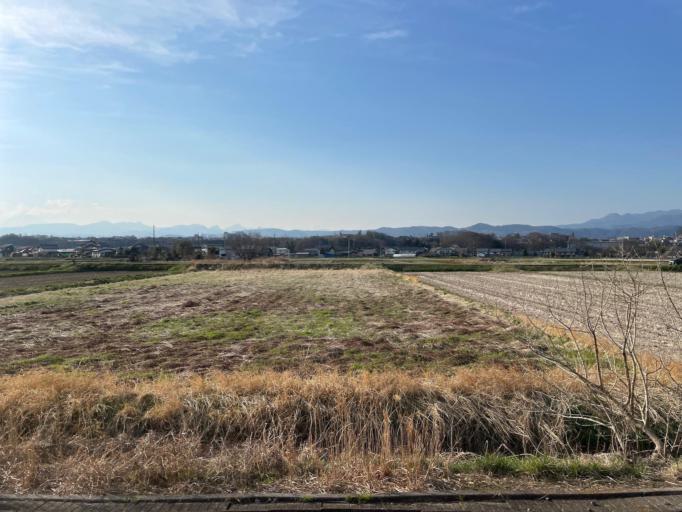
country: JP
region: Gunma
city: Annaka
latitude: 36.3101
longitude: 138.8792
